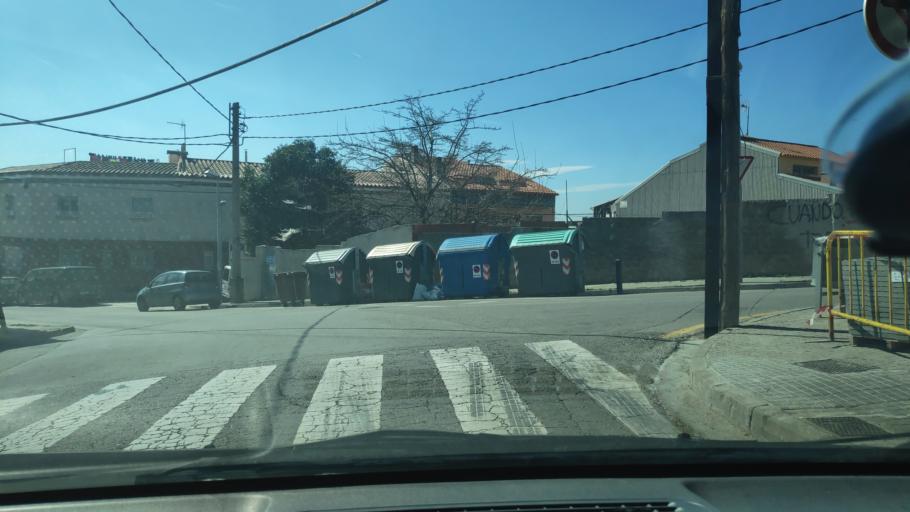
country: ES
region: Catalonia
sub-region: Provincia de Barcelona
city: Rubi
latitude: 41.4997
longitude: 2.0439
